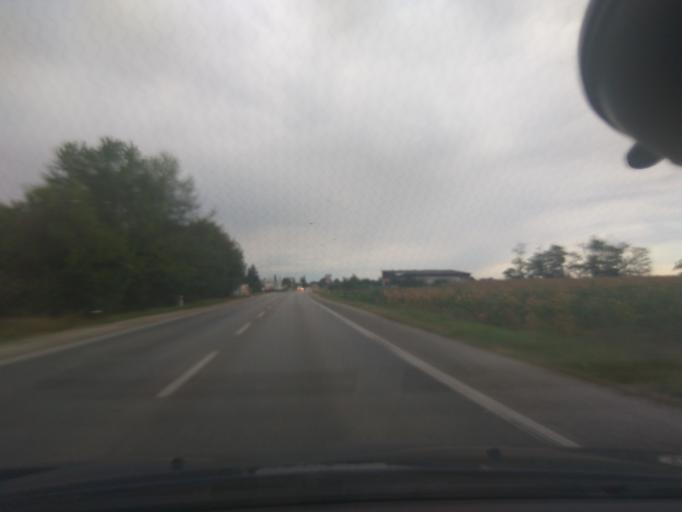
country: SK
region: Trnavsky
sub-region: Okres Trnava
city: Piestany
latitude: 48.6180
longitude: 17.8361
